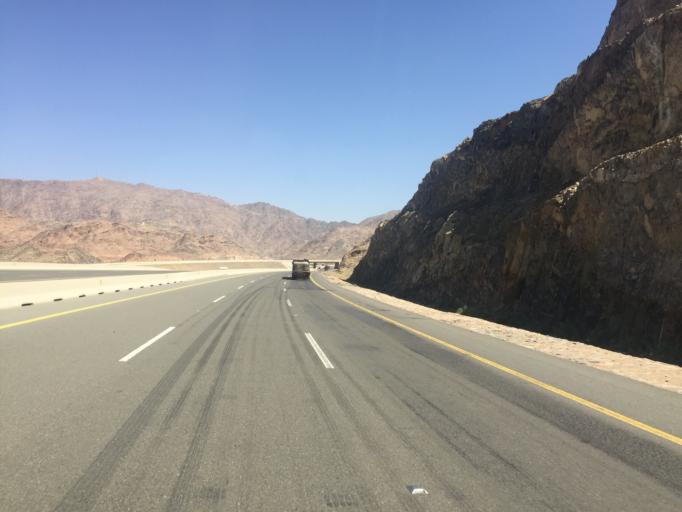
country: SA
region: Al Madinah al Munawwarah
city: Badr Hunayn
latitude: 24.0884
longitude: 39.1011
